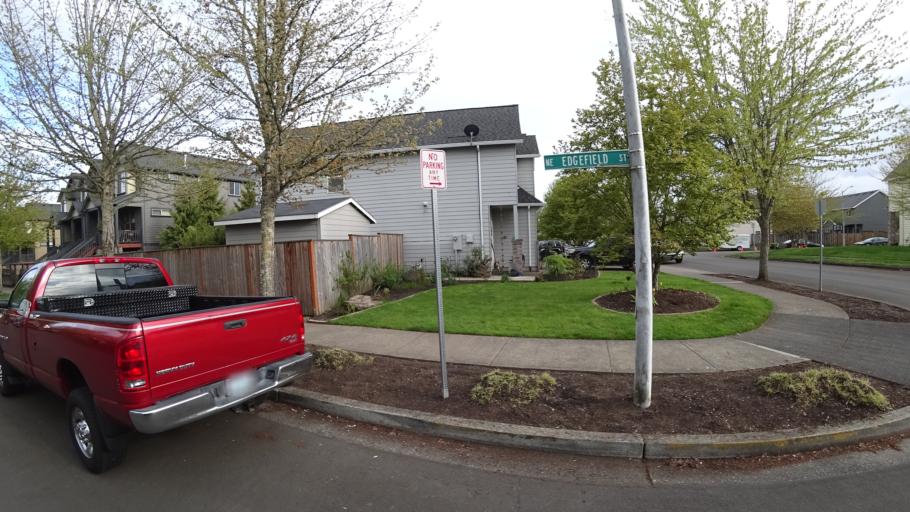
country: US
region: Oregon
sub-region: Washington County
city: Hillsboro
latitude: 45.5485
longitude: -122.9688
